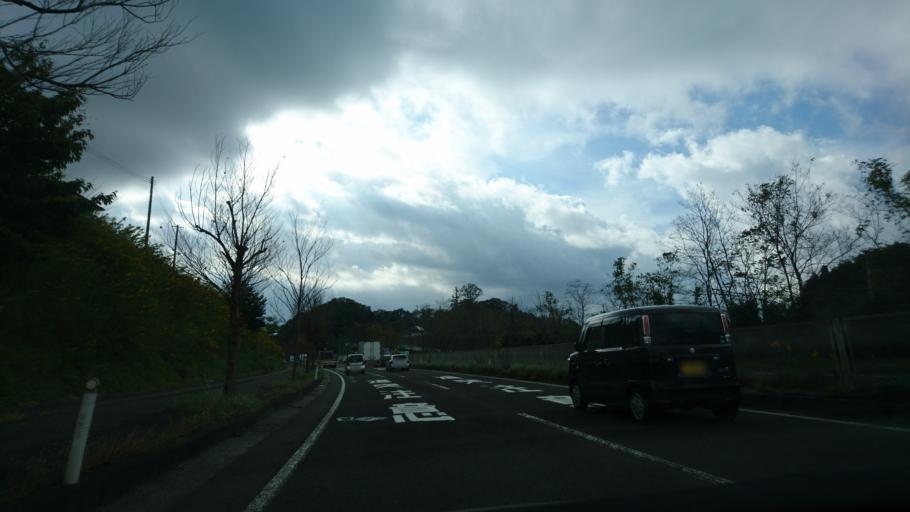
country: JP
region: Miyagi
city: Tomiya
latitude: 38.3793
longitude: 140.8726
